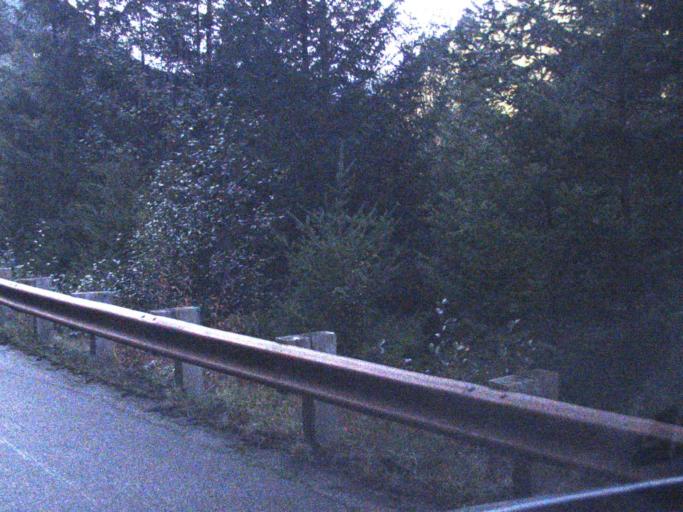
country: US
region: Washington
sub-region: Snohomish County
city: Darrington
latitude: 48.7053
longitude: -120.9667
